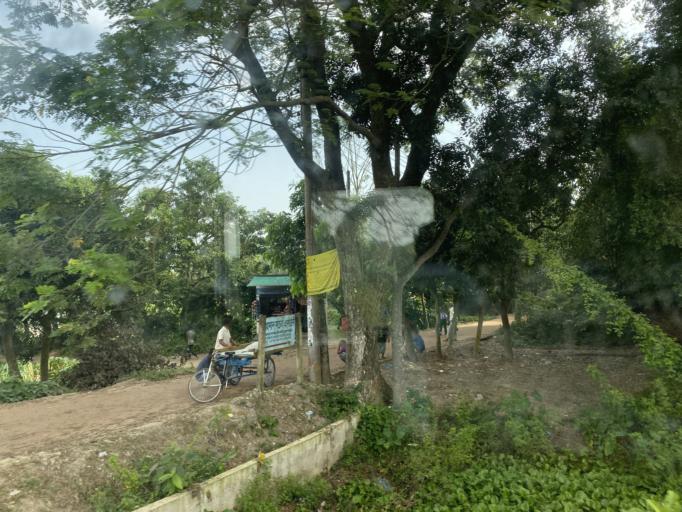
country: BD
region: Chittagong
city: Nabinagar
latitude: 23.9459
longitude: 91.1207
